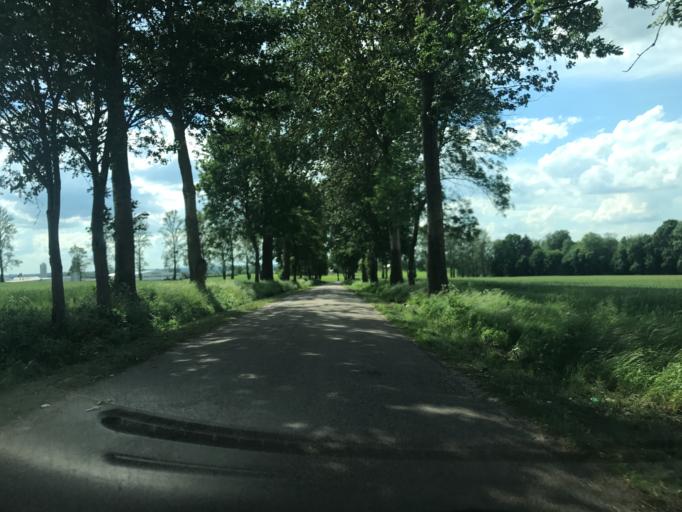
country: PL
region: Warmian-Masurian Voivodeship
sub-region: Powiat ilawski
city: Lubawa
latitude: 53.4213
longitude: 19.7884
